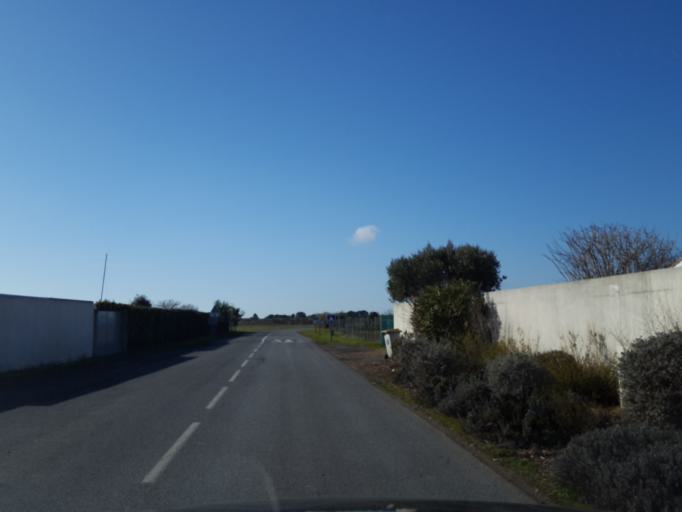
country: FR
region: Poitou-Charentes
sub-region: Departement de la Charente-Maritime
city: La Couarde-sur-Mer
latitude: 46.2213
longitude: -1.4418
